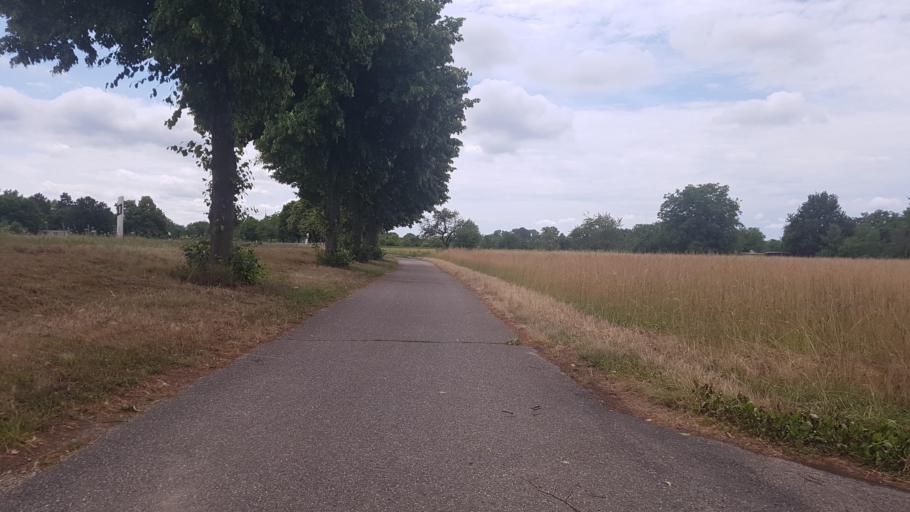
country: DE
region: Baden-Wuerttemberg
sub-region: Karlsruhe Region
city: Iffezheim
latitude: 48.8522
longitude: 8.1417
